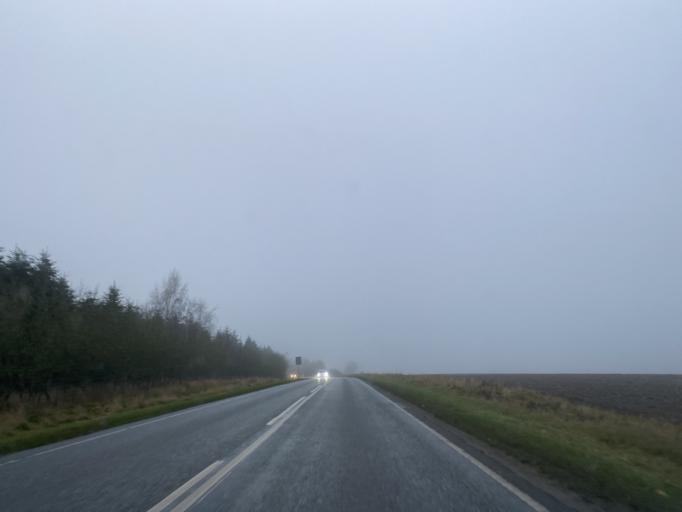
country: DK
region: Central Jutland
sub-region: Arhus Kommune
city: Solbjerg
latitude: 55.9816
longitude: 10.0470
